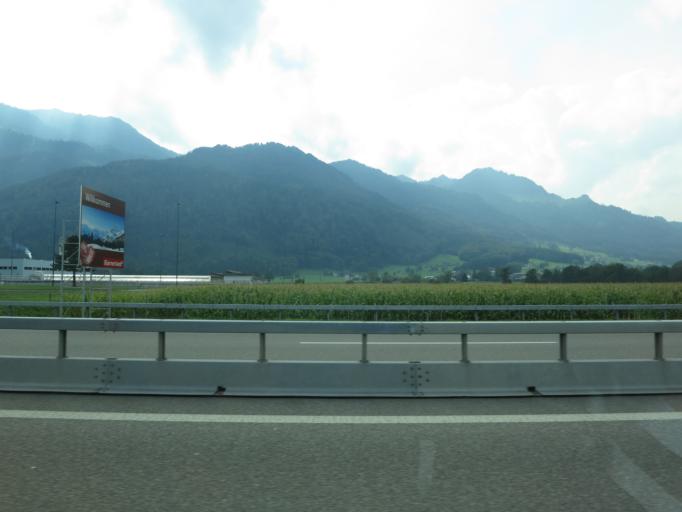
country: CH
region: Glarus
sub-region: Glarus
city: Bilten
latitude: 47.1672
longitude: 9.0137
